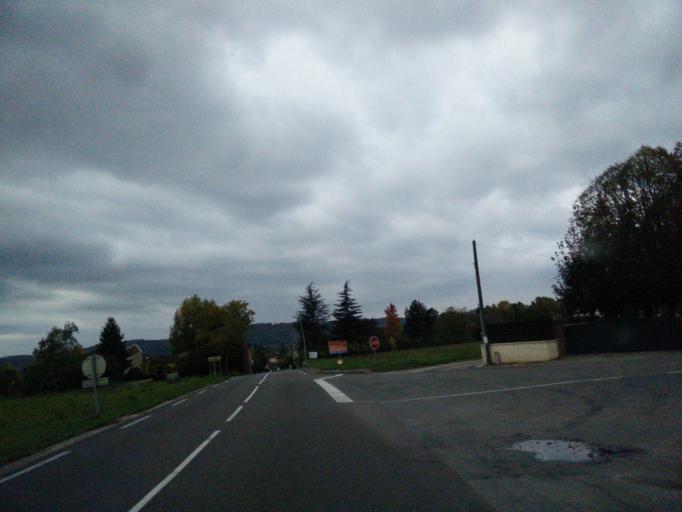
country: FR
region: Midi-Pyrenees
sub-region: Departement du Lot
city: Prayssac
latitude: 44.4992
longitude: 1.1971
